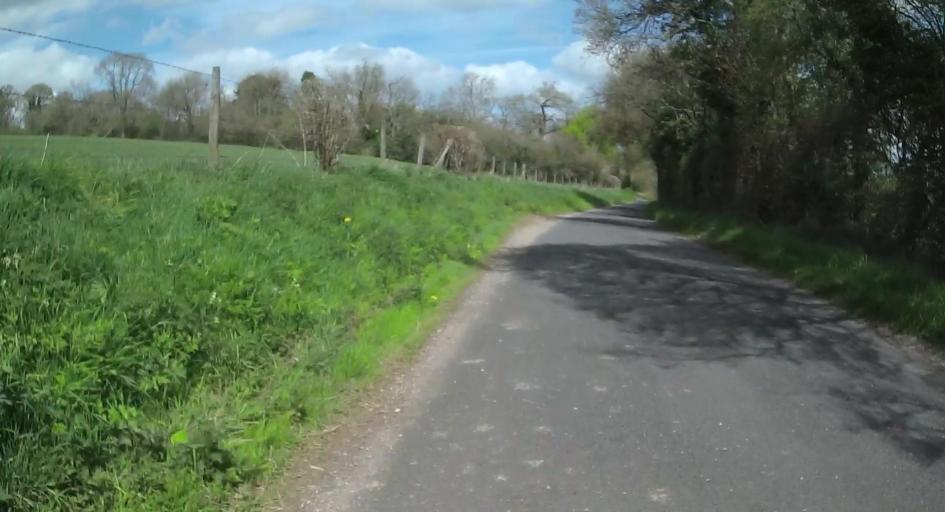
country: GB
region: England
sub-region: Hampshire
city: Romsey
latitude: 51.0701
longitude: -1.5265
